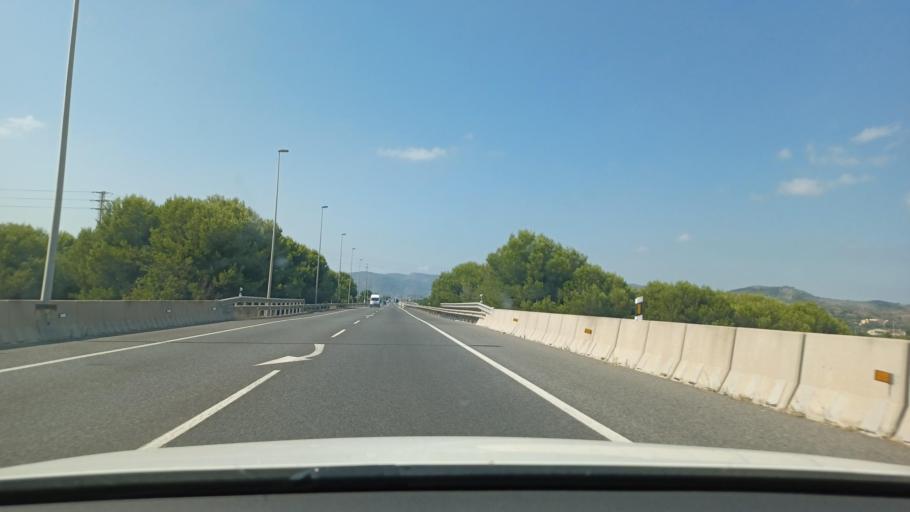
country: ES
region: Valencia
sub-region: Provincia de Castello
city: Almassora
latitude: 39.9830
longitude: -0.0879
